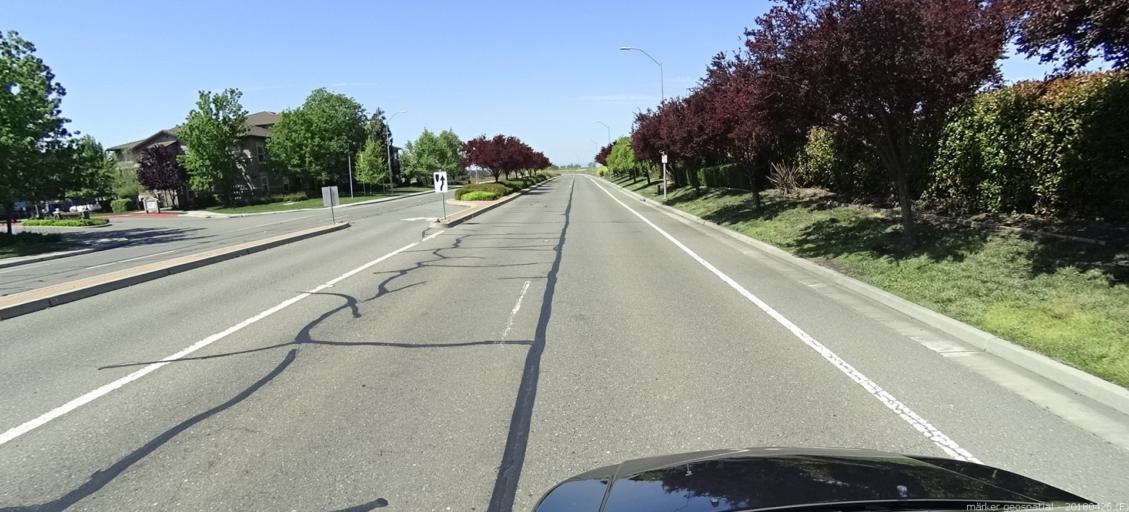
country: US
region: California
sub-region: Yolo County
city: West Sacramento
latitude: 38.5451
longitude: -121.5707
